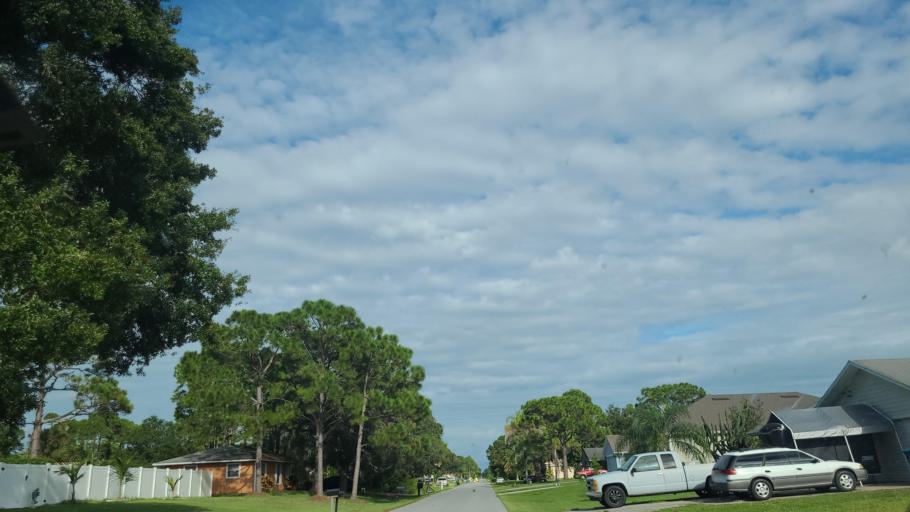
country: US
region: Florida
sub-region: Brevard County
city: Palm Bay
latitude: 27.9837
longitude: -80.6595
